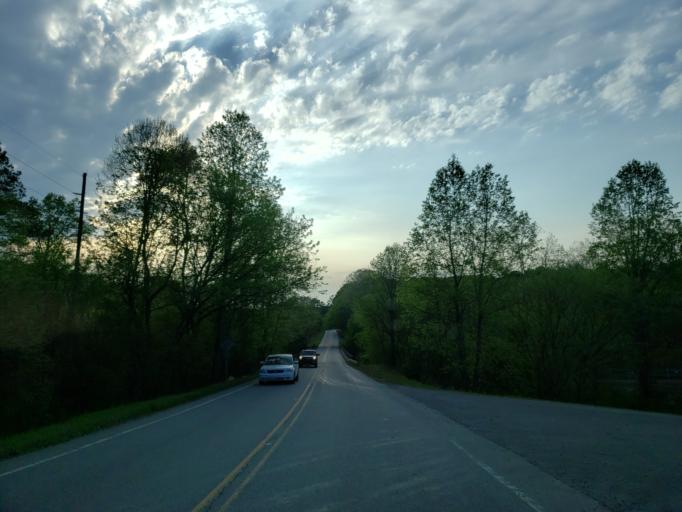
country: US
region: Georgia
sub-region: Cherokee County
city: Ball Ground
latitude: 34.2986
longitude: -84.3953
